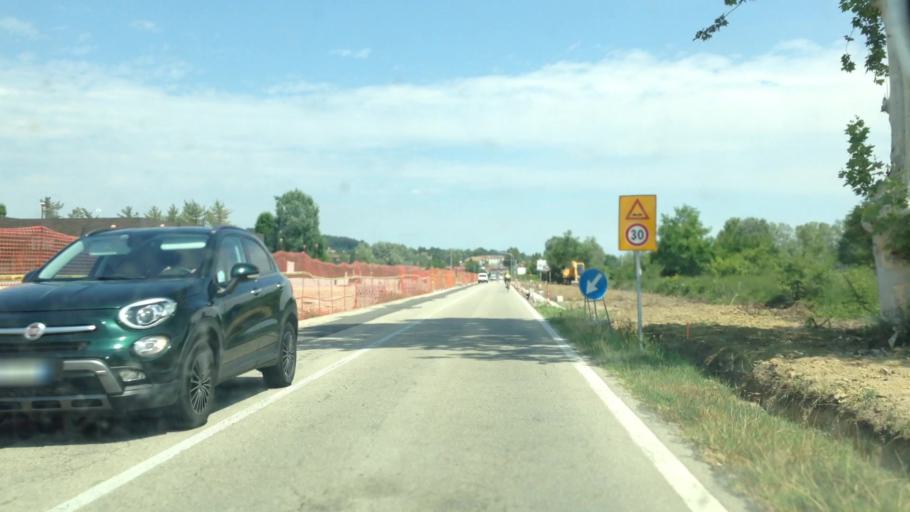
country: IT
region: Piedmont
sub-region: Provincia di Asti
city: Portacomaro
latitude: 44.9484
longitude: 8.2237
